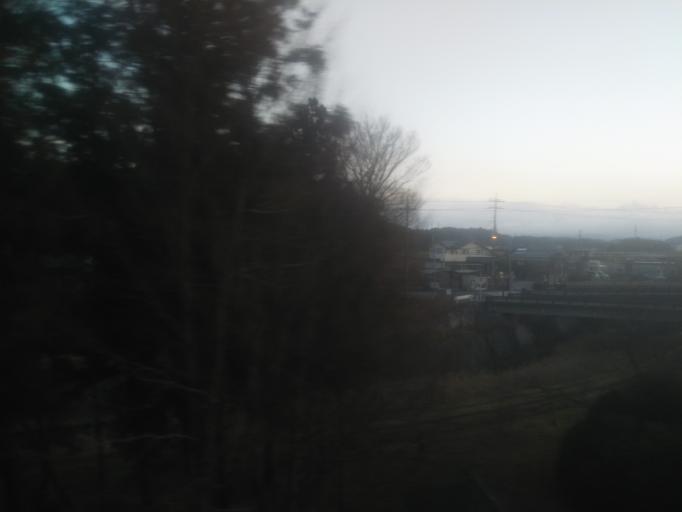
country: JP
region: Shiga Prefecture
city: Minakuchicho-matoba
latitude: 34.9053
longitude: 136.2069
